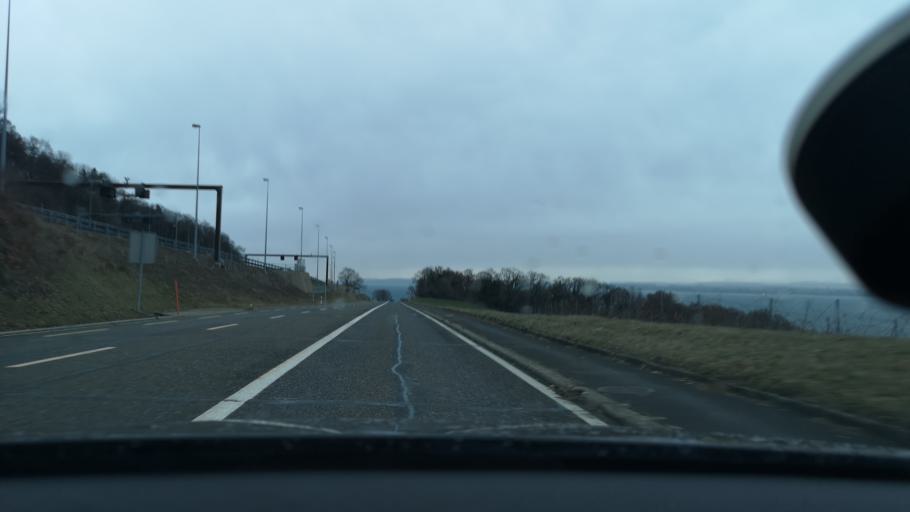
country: CH
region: Neuchatel
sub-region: Boudry District
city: Saint-Aubin-Sauges
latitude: 46.8611
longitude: 6.7408
